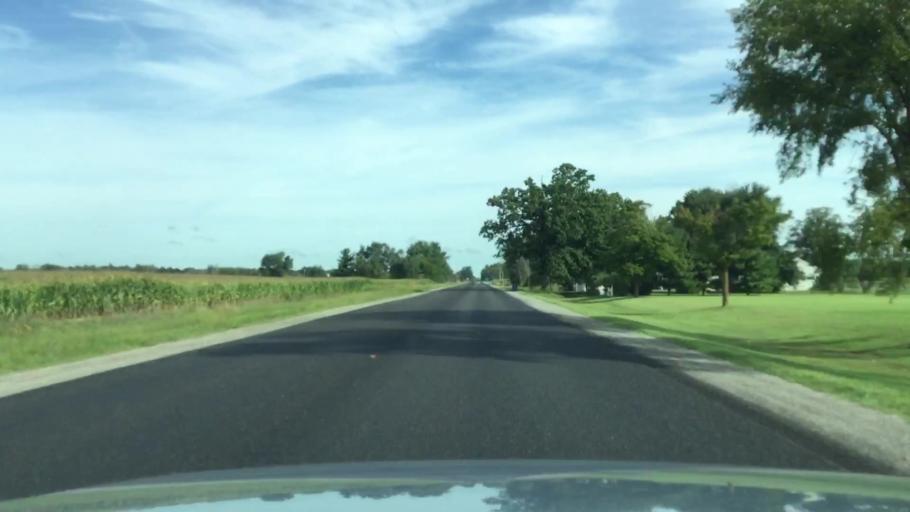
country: US
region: Michigan
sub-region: Genesee County
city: Montrose
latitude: 43.1387
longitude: -83.9293
